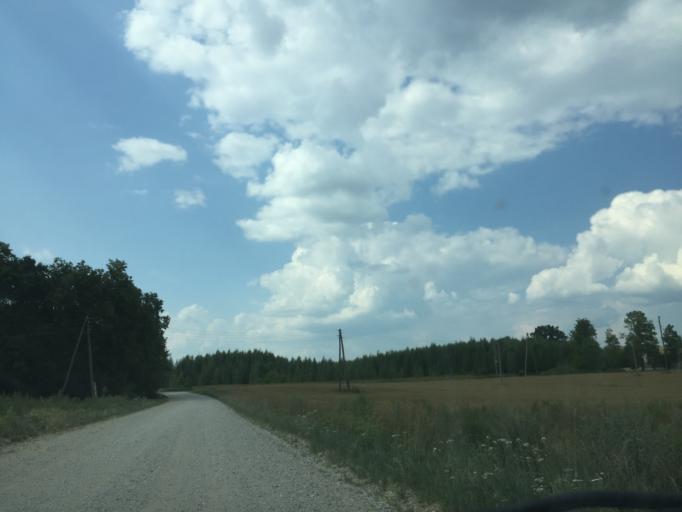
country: LV
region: Auces Novads
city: Auce
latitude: 56.4091
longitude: 23.0344
